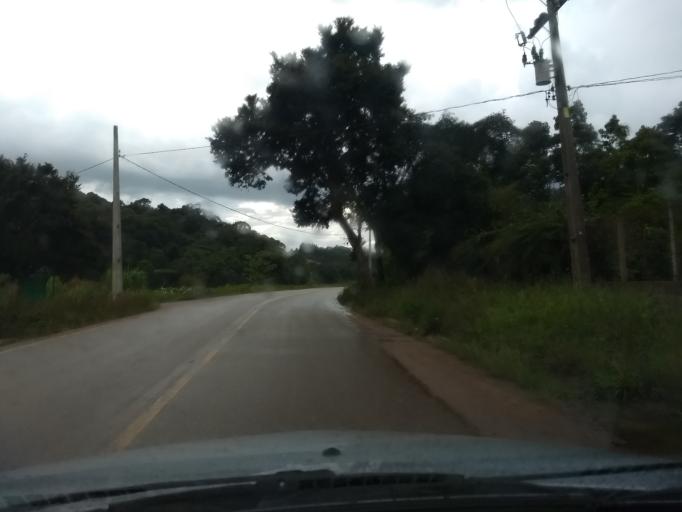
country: BR
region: Minas Gerais
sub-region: Extrema
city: Extrema
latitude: -22.7610
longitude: -46.3385
